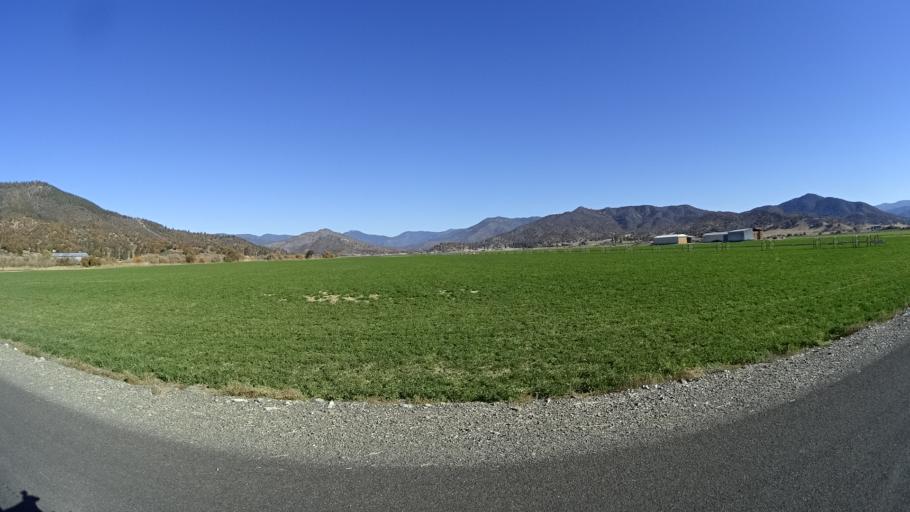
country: US
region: California
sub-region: Siskiyou County
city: Yreka
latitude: 41.5752
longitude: -122.8566
